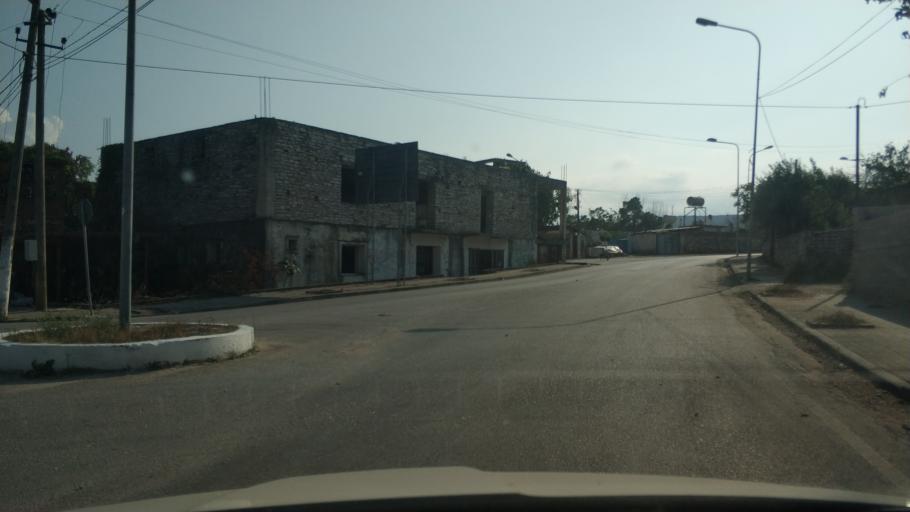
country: AL
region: Vlore
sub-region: Rrethi i Sarandes
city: Aliko
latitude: 39.8421
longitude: 20.0376
